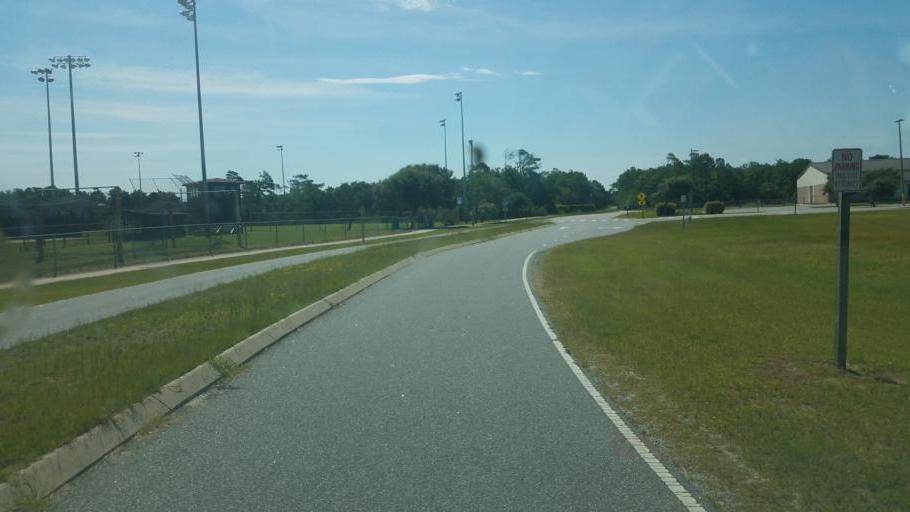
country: US
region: North Carolina
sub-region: Dare County
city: Kill Devil Hills
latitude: 36.0079
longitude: -75.6639
